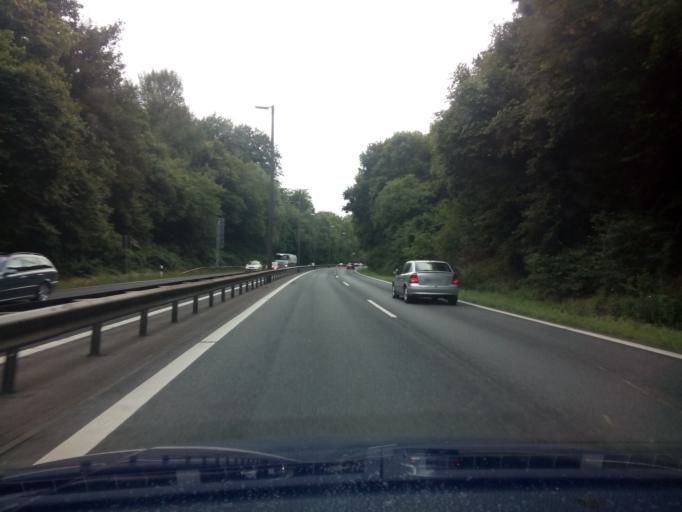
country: DE
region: Lower Saxony
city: Lemwerder
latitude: 53.1728
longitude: 8.6732
